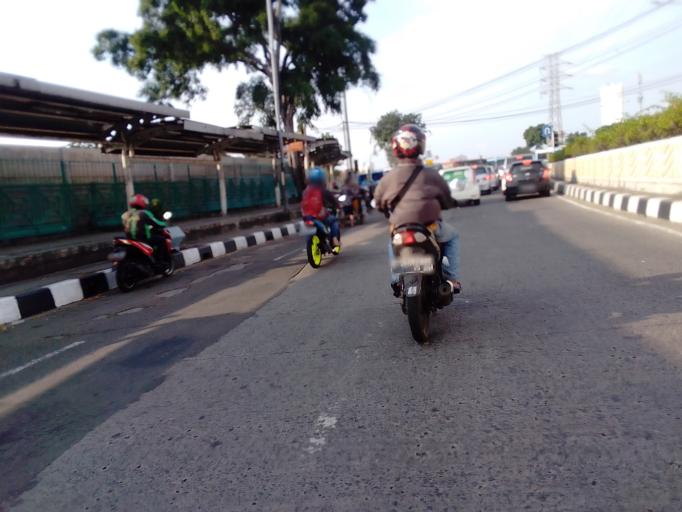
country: ID
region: Jakarta Raya
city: Jakarta
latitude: -6.1772
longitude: 106.8435
